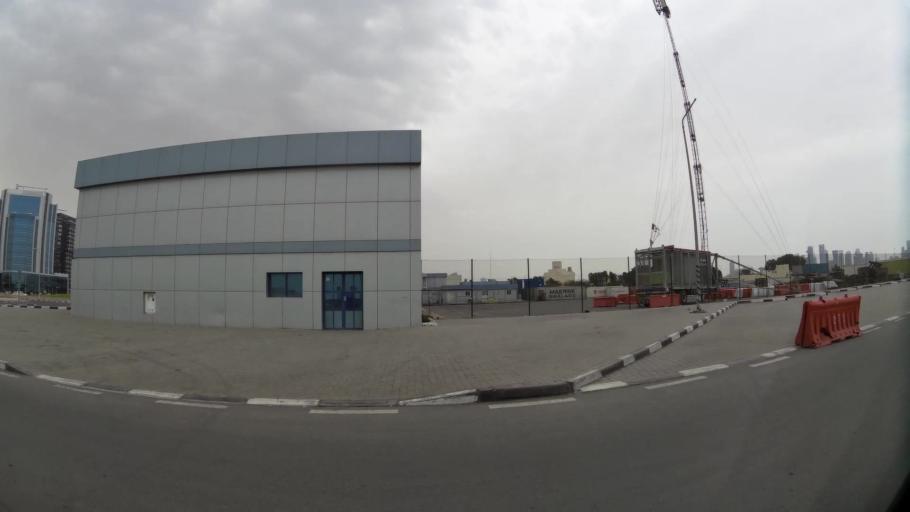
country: QA
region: Baladiyat ad Dawhah
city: Doha
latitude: 25.2943
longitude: 51.5463
